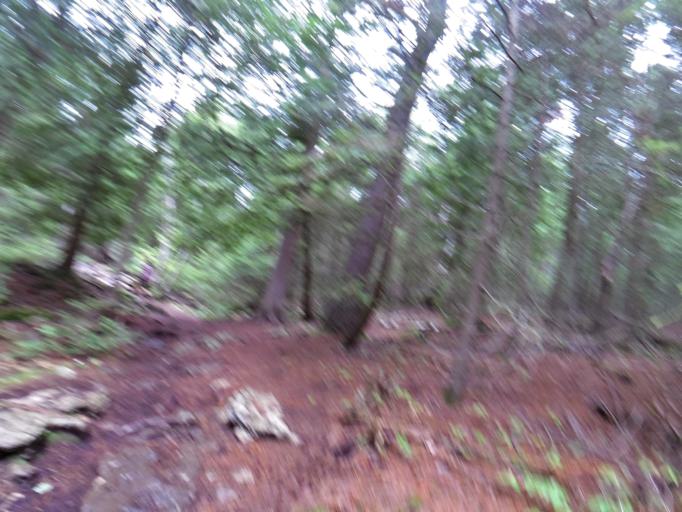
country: CA
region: Ontario
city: Tobermory
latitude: 45.2611
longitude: -81.6482
